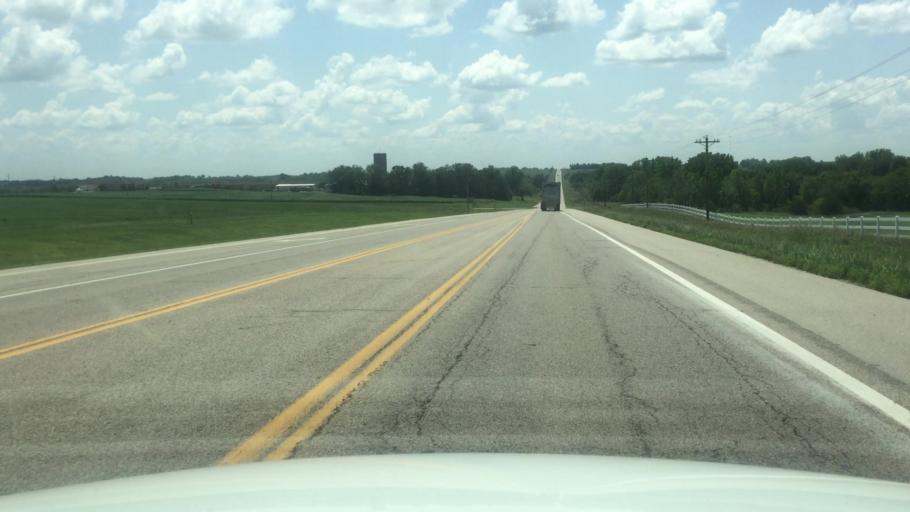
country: US
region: Kansas
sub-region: Brown County
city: Horton
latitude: 39.6991
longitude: -95.7303
